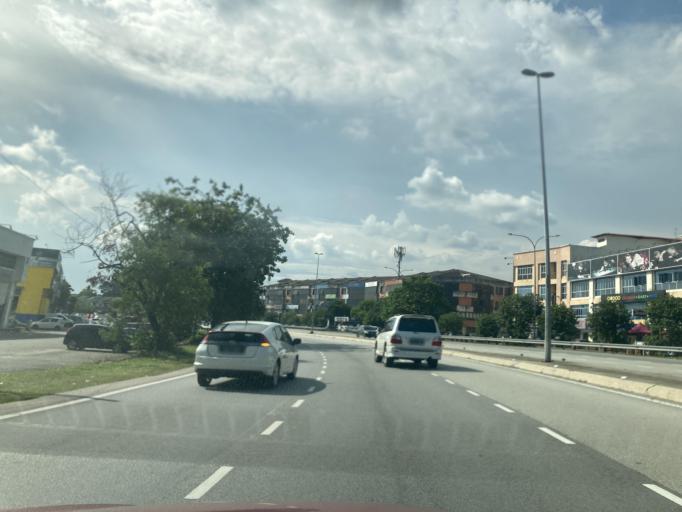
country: MY
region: Selangor
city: Kampung Baru Subang
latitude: 3.1488
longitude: 101.5440
